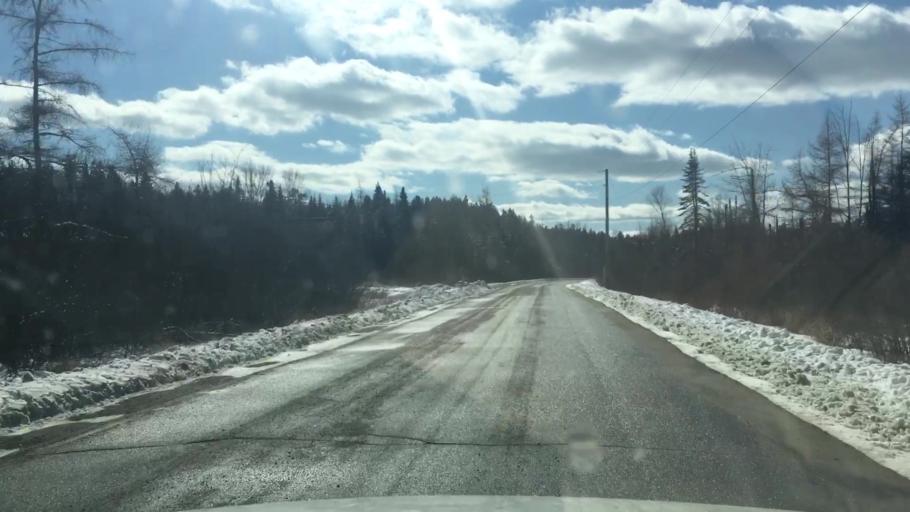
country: US
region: Maine
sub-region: Washington County
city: Machiasport
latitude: 44.6781
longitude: -67.4160
